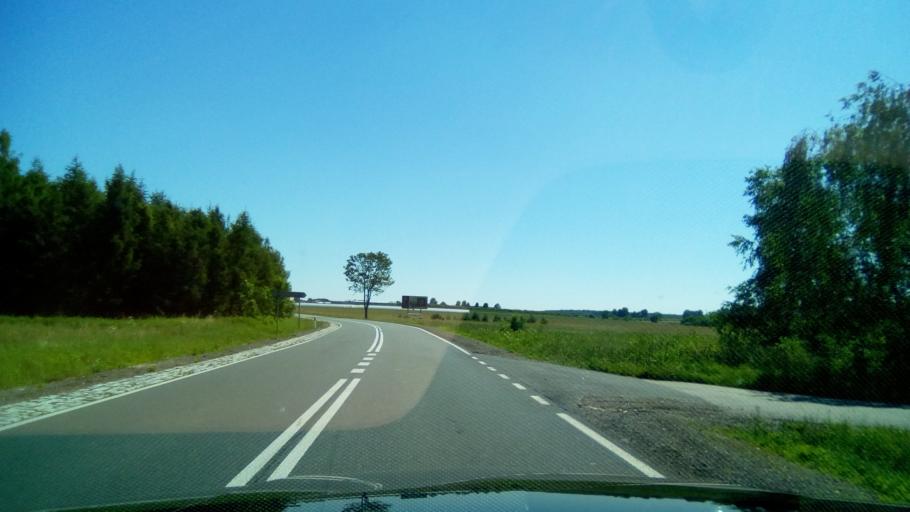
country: PL
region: Masovian Voivodeship
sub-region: Powiat przysuski
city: Klwow
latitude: 51.5292
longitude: 20.6146
